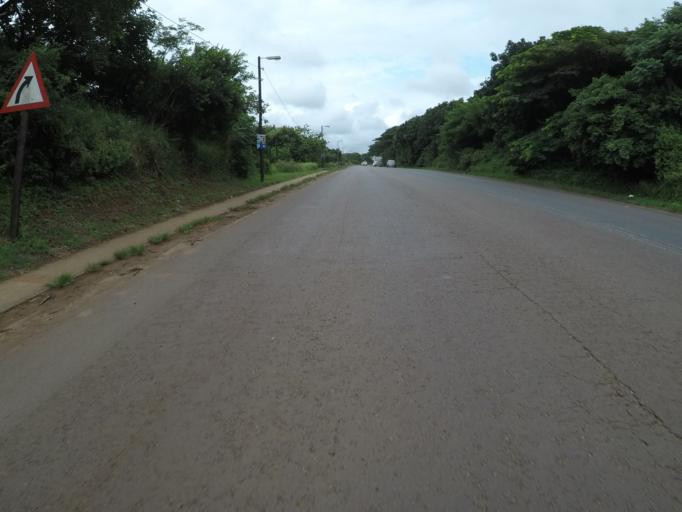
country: ZA
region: KwaZulu-Natal
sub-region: uThungulu District Municipality
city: Empangeni
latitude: -28.7766
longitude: 31.8849
